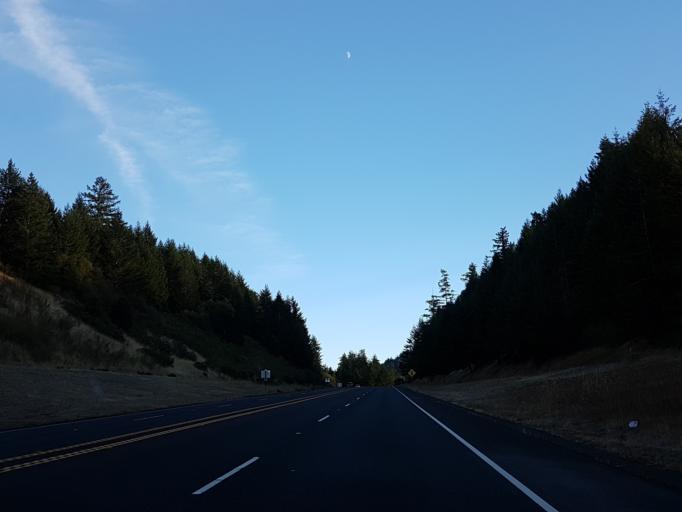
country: US
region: California
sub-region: Humboldt County
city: Redway
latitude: 39.9439
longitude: -123.7793
